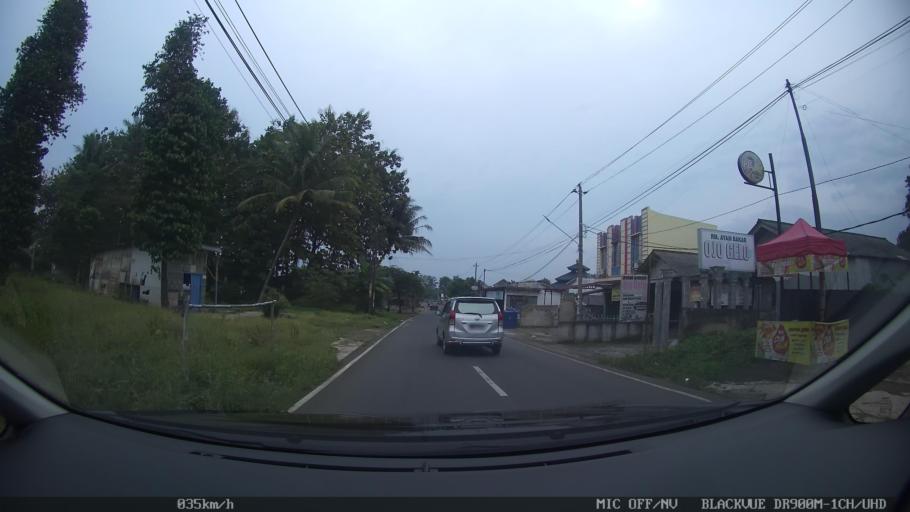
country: ID
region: Lampung
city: Kedaton
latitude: -5.3879
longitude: 105.2408
